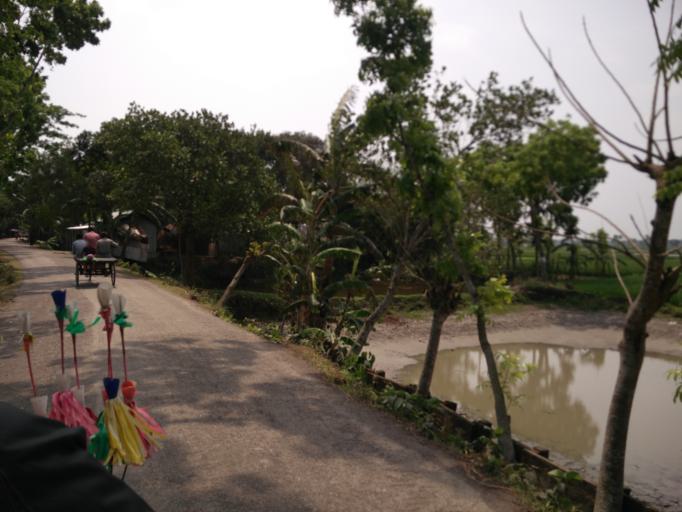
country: BD
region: Dhaka
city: Sherpur
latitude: 24.9370
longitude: 90.1590
